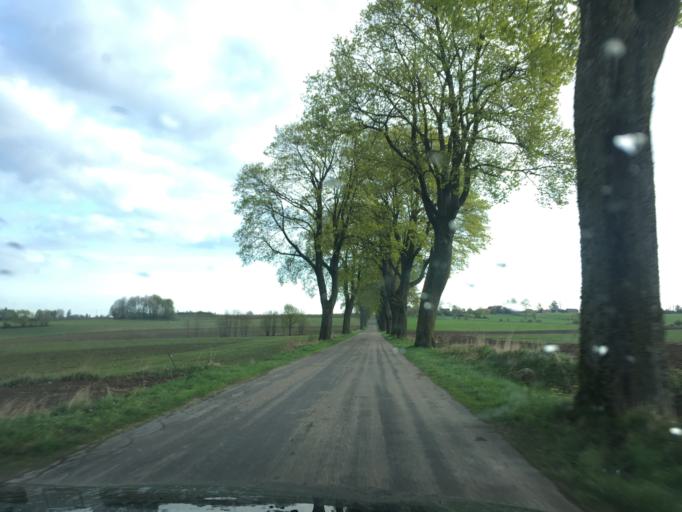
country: PL
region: Warmian-Masurian Voivodeship
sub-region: Powiat ostrodzki
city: Dabrowno
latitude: 53.4318
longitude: 19.9753
